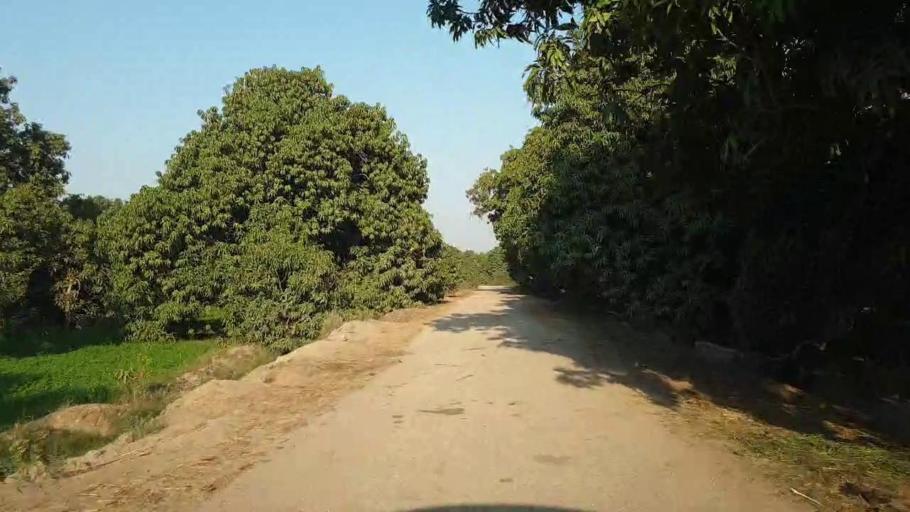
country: PK
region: Sindh
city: Mirpur Khas
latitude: 25.4411
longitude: 68.9123
